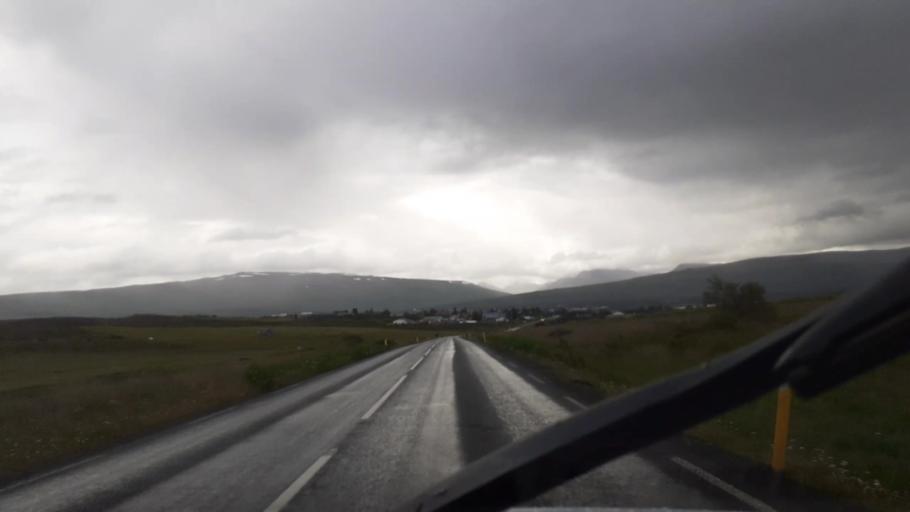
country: IS
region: East
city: Egilsstadir
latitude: 65.2947
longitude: -14.4405
